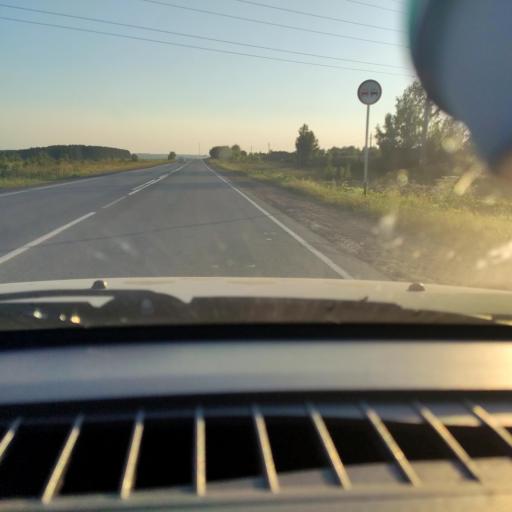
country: RU
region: Perm
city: Kungur
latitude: 57.4494
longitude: 56.9988
